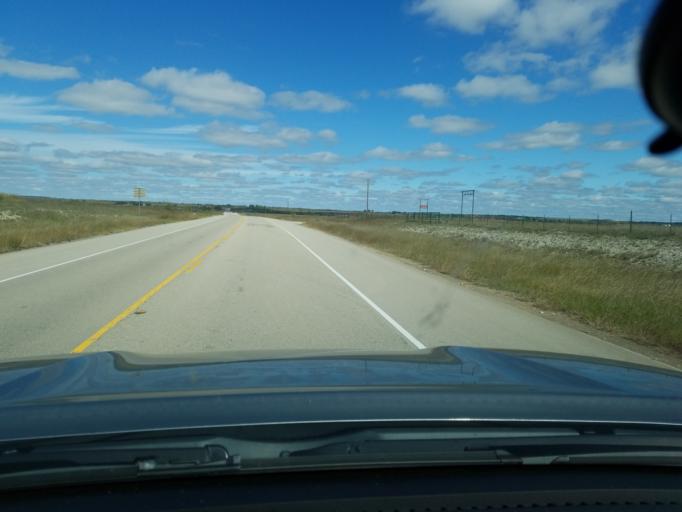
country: US
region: Texas
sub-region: Hamilton County
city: Hamilton
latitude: 31.6301
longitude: -98.1530
